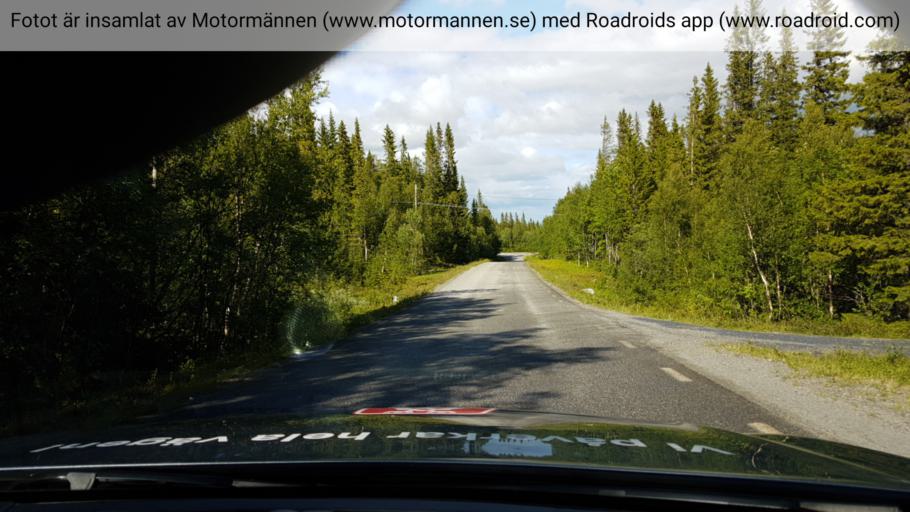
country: SE
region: Jaemtland
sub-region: Bergs Kommun
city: Hoverberg
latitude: 63.0157
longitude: 13.9434
